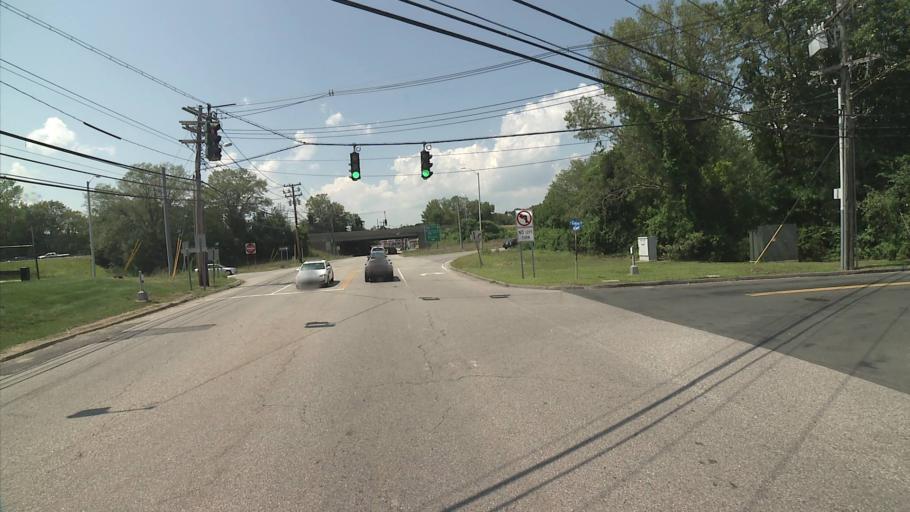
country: US
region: Connecticut
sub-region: New London County
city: Norwich
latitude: 41.5527
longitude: -72.1045
